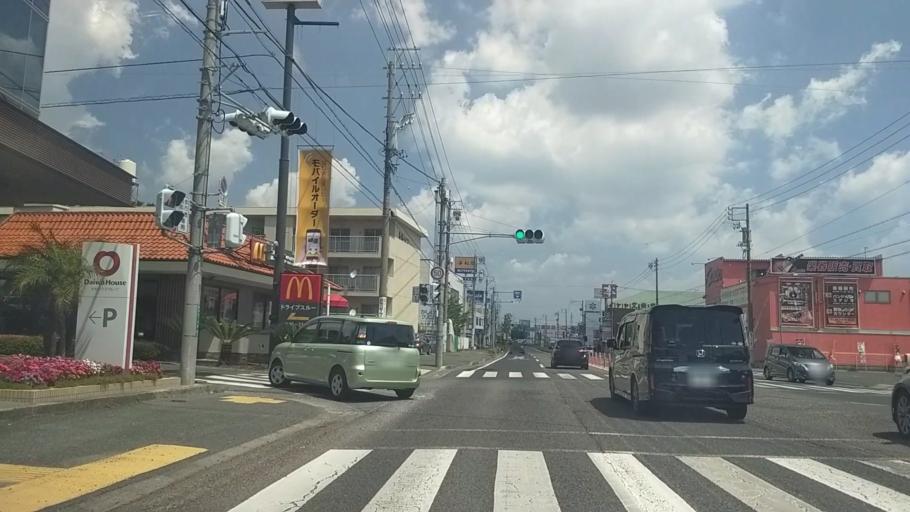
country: JP
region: Shizuoka
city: Hamamatsu
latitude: 34.7290
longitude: 137.7324
